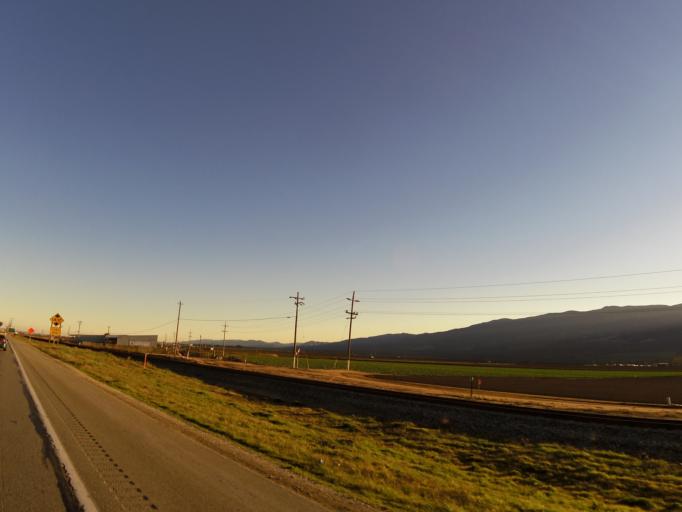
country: US
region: California
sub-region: Monterey County
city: Gonzales
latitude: 36.4698
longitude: -121.3965
